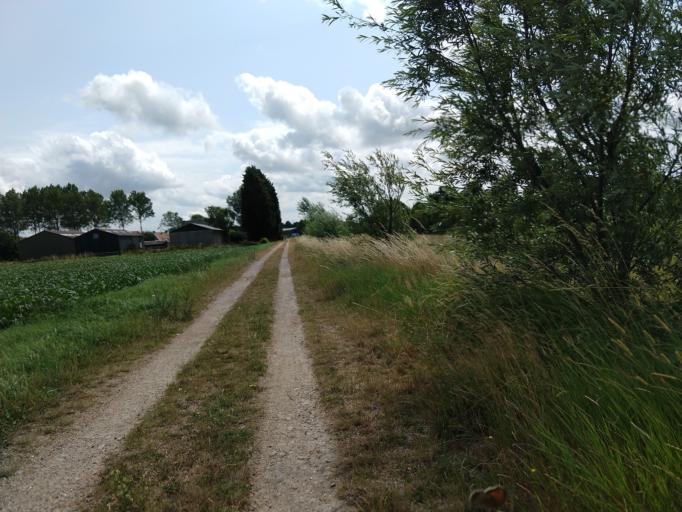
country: NL
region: Zeeland
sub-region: Gemeente Goes
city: Goes
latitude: 51.4801
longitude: 3.8108
